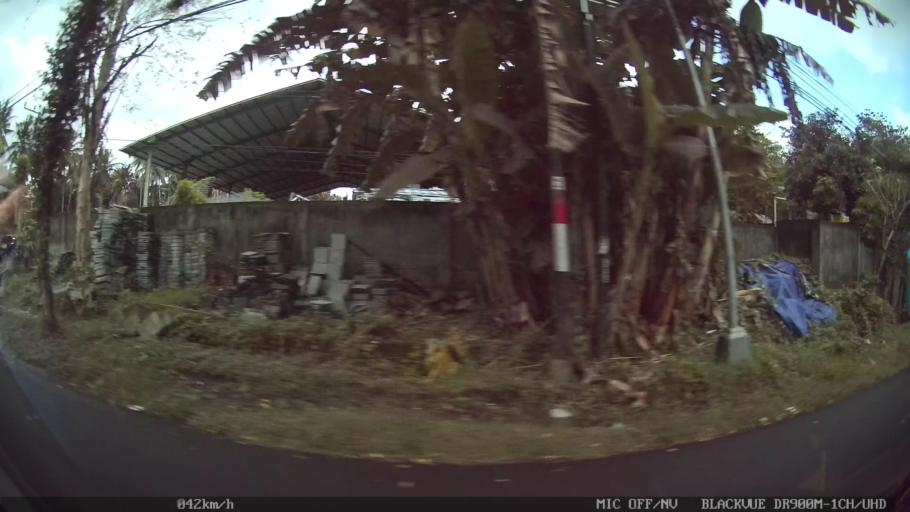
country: ID
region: Bali
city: Banjar Parekan
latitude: -8.5694
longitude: 115.2081
